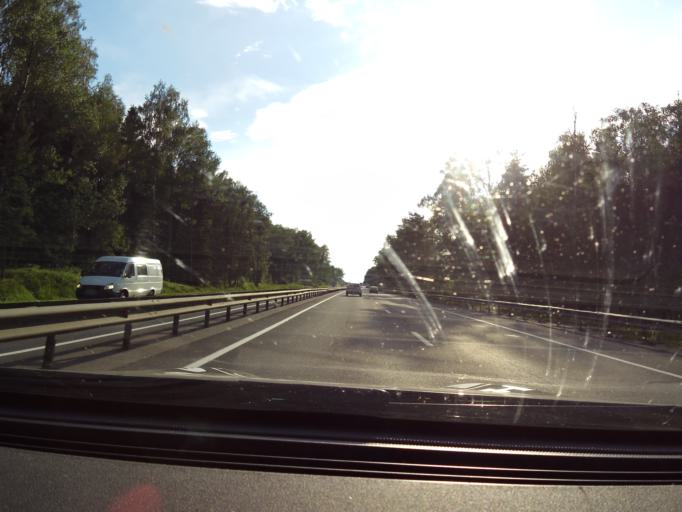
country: RU
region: Vladimir
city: Melekhovo
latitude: 56.2092
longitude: 41.2576
